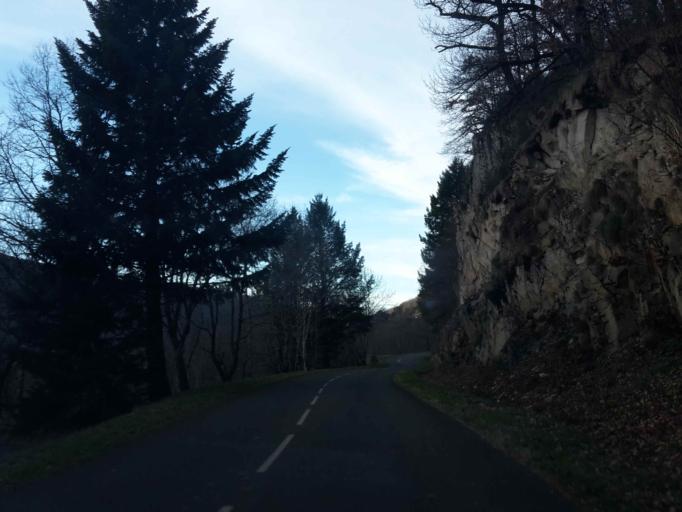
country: FR
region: Auvergne
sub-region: Departement du Cantal
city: Riom-es-Montagnes
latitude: 45.1853
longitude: 2.5789
